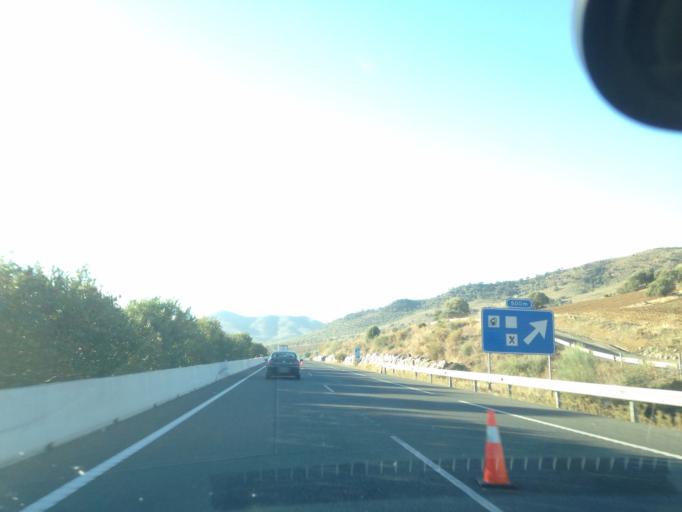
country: ES
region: Andalusia
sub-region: Provincia de Malaga
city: Casabermeja
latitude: 36.9304
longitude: -4.4464
